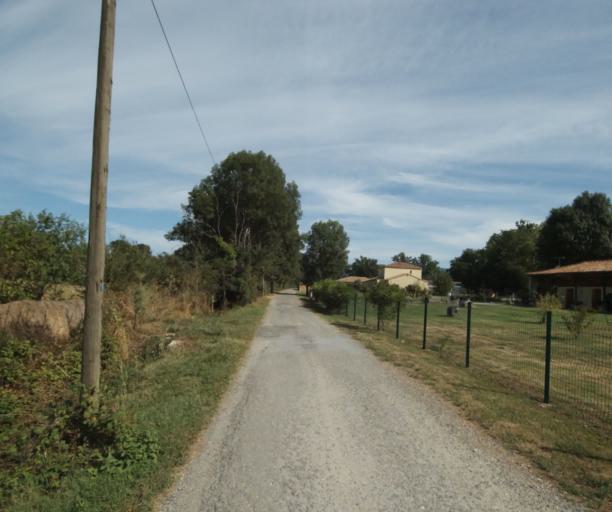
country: FR
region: Midi-Pyrenees
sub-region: Departement du Tarn
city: Soual
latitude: 43.5227
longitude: 2.0952
